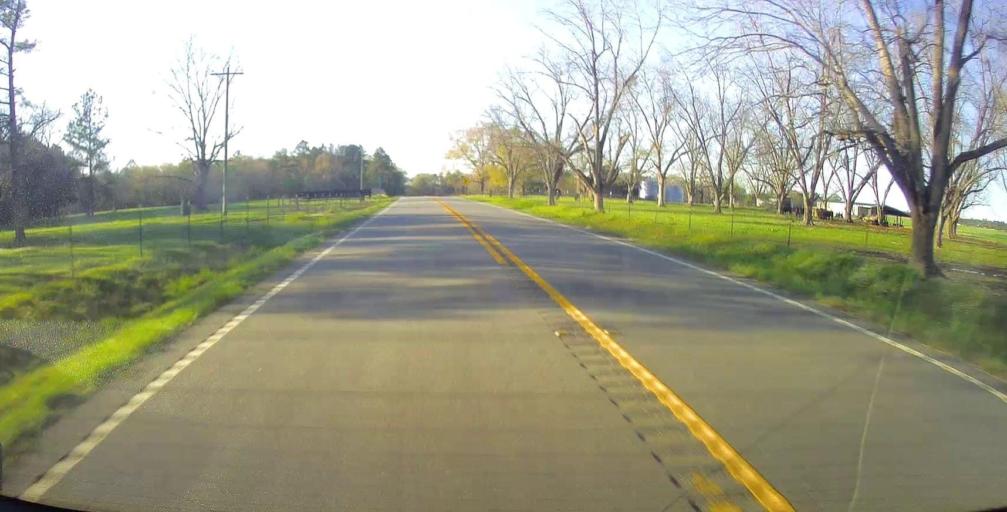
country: US
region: Georgia
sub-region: Wilcox County
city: Abbeville
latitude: 32.1540
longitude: -83.3510
